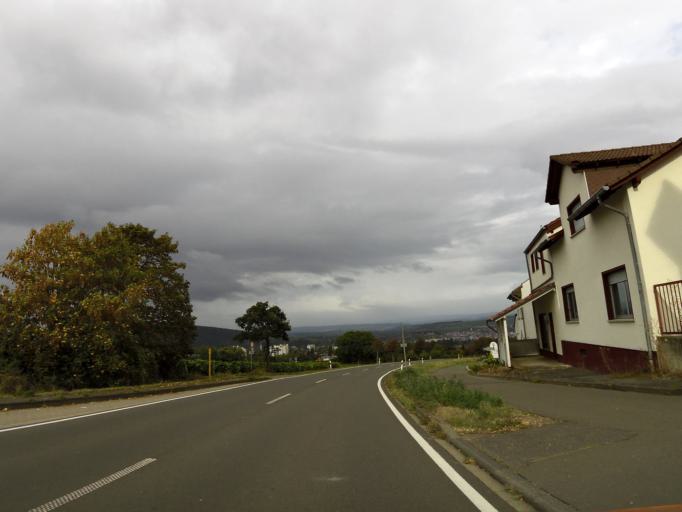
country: DE
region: Rheinland-Pfalz
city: Hackenheim
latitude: 49.8277
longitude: 7.8897
